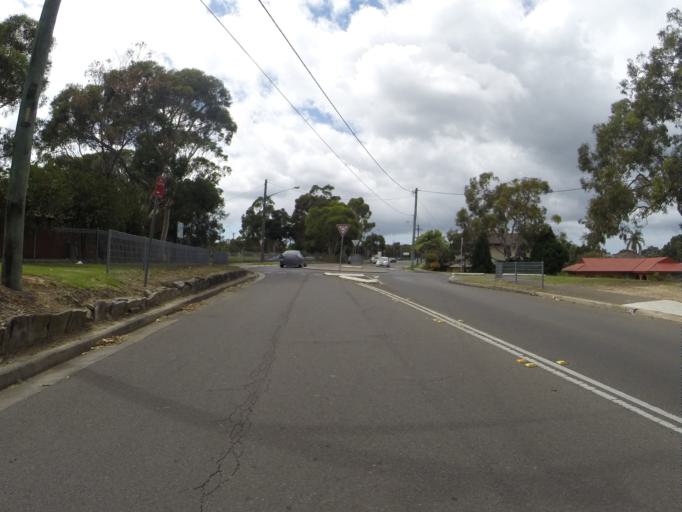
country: AU
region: New South Wales
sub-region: Sutherland Shire
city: Engadine
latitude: -34.0735
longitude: 151.0104
